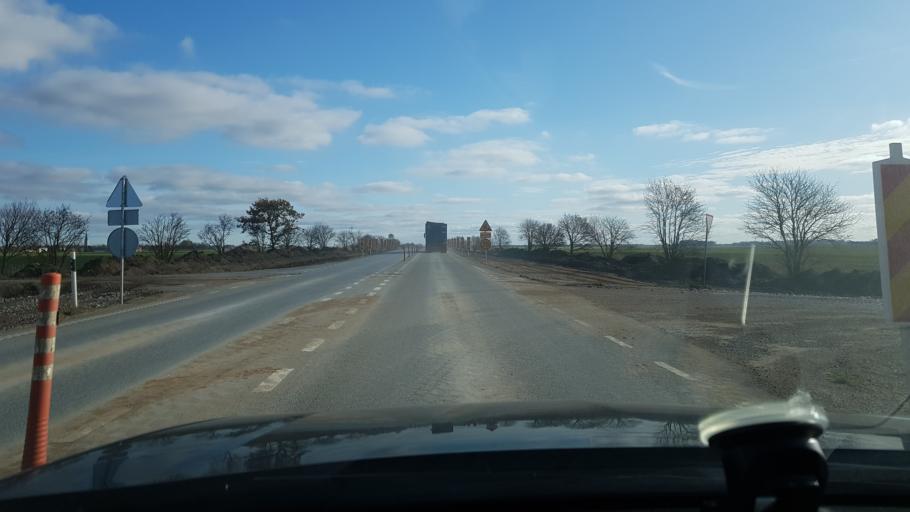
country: EE
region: Laeaene-Virumaa
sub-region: Haljala vald
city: Haljala
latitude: 59.4278
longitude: 26.2355
